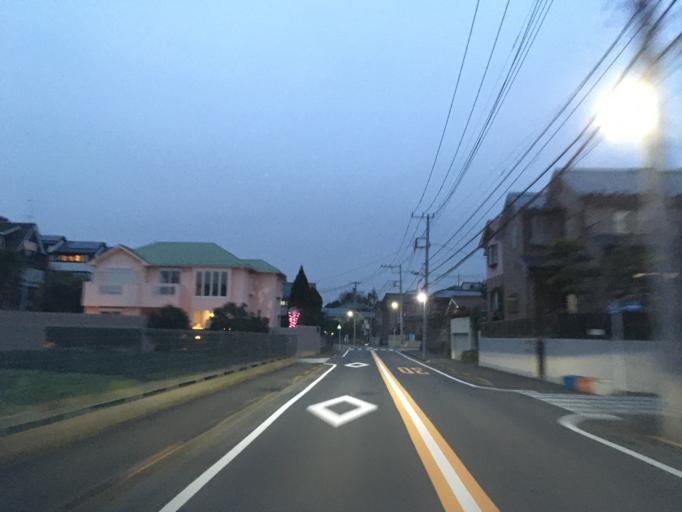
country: JP
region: Tokyo
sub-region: Machida-shi
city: Machida
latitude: 35.5207
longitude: 139.4791
